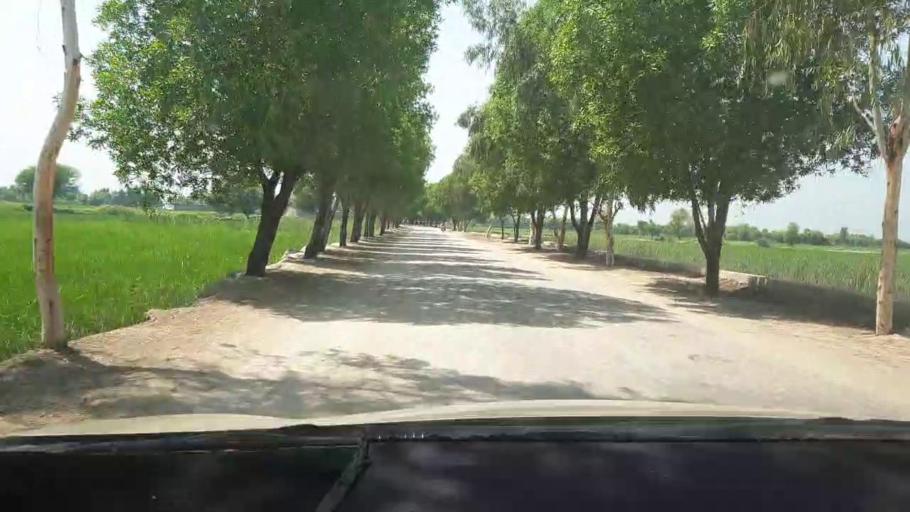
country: PK
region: Sindh
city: Miro Khan
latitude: 27.6718
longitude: 68.0554
